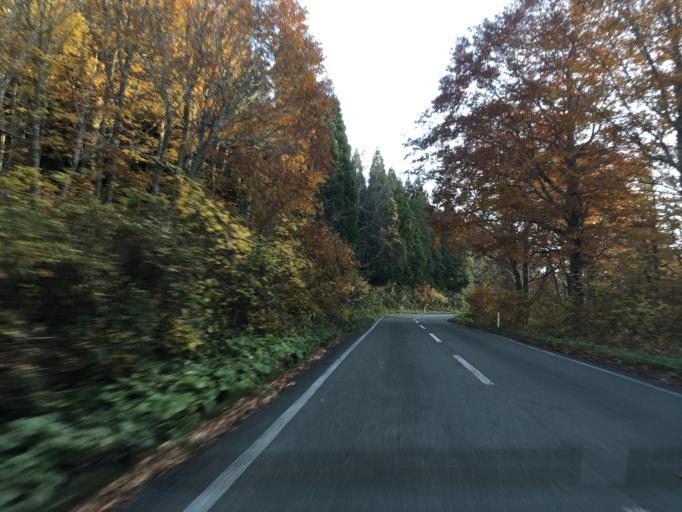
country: JP
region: Akita
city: Yuzawa
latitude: 38.9629
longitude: 140.7139
